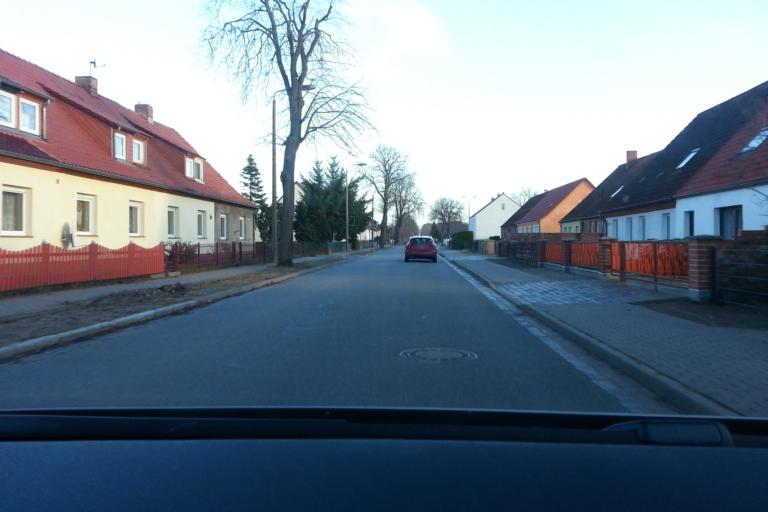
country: DE
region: Mecklenburg-Vorpommern
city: Ferdinandshof
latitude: 53.6634
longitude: 13.8955
